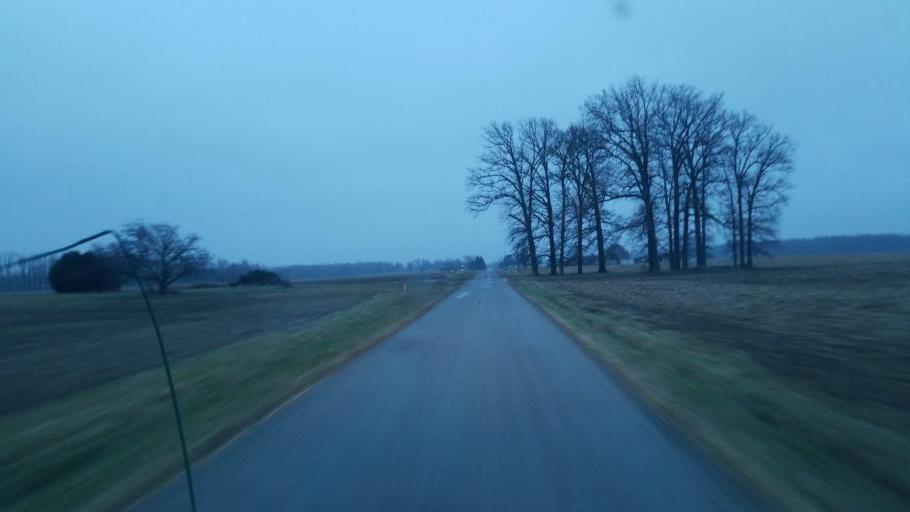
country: US
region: Ohio
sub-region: Delaware County
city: Ashley
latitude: 40.4288
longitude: -82.9383
